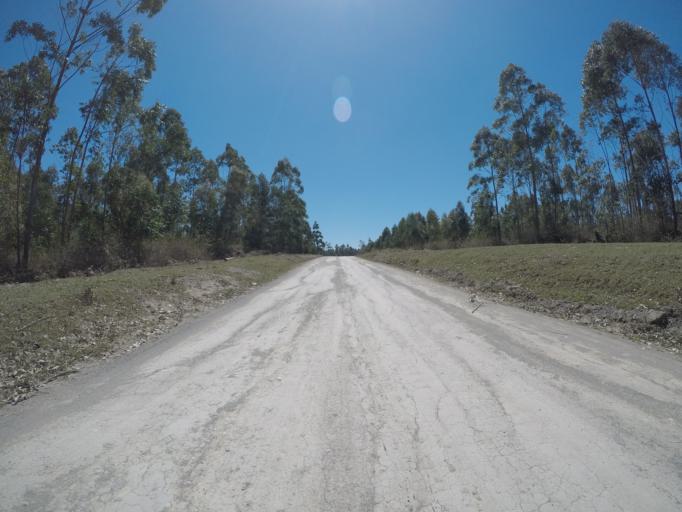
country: ZA
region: Eastern Cape
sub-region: OR Tambo District Municipality
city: Libode
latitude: -31.9552
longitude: 29.0232
